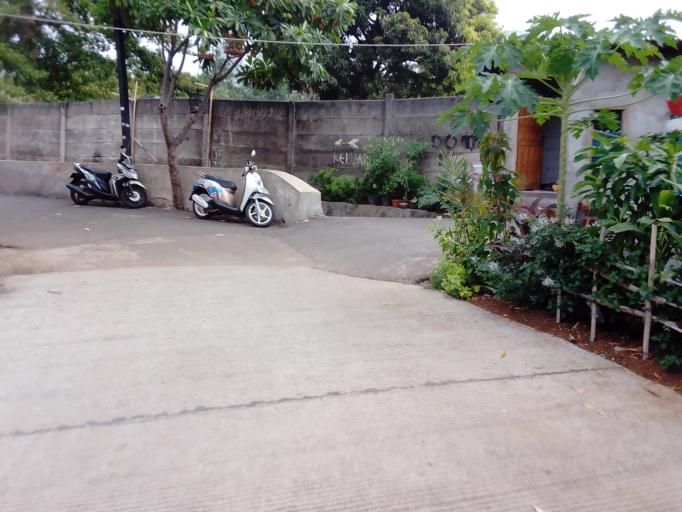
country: ID
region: Jakarta Raya
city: Jakarta
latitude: -6.1997
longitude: 106.8055
